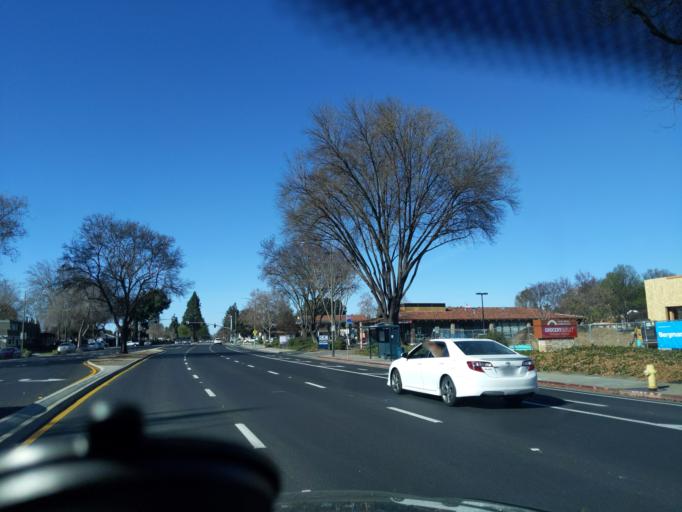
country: US
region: California
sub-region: Santa Clara County
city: Seven Trees
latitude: 37.2260
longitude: -121.7752
